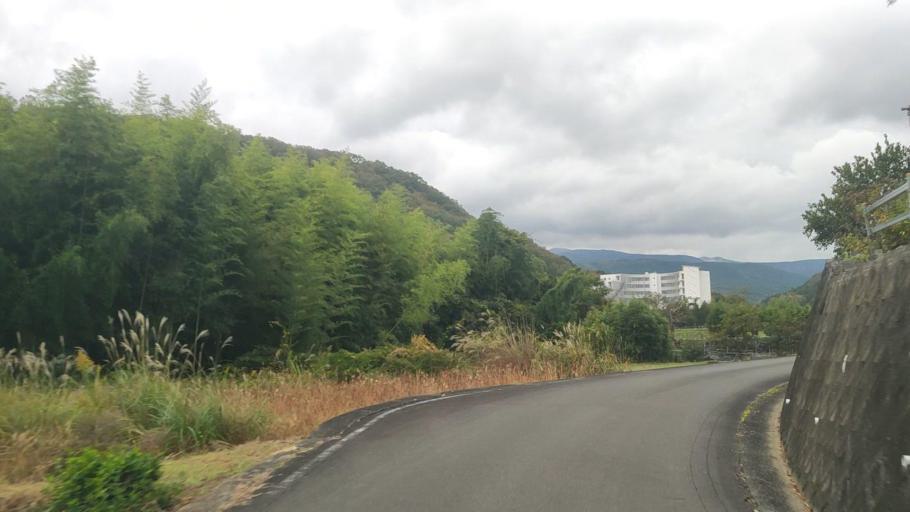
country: JP
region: Shizuoka
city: Ito
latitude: 34.9351
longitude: 138.9940
